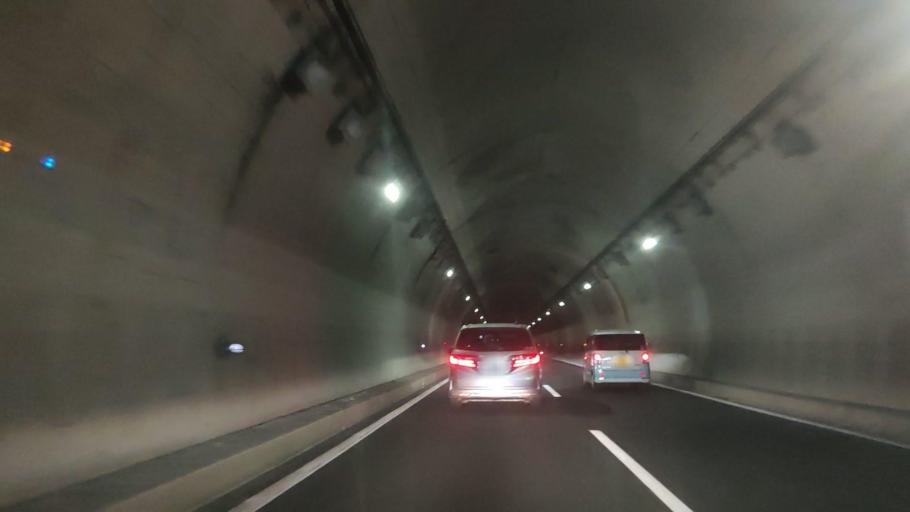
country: JP
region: Nagasaki
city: Obita
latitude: 32.8131
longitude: 129.9303
